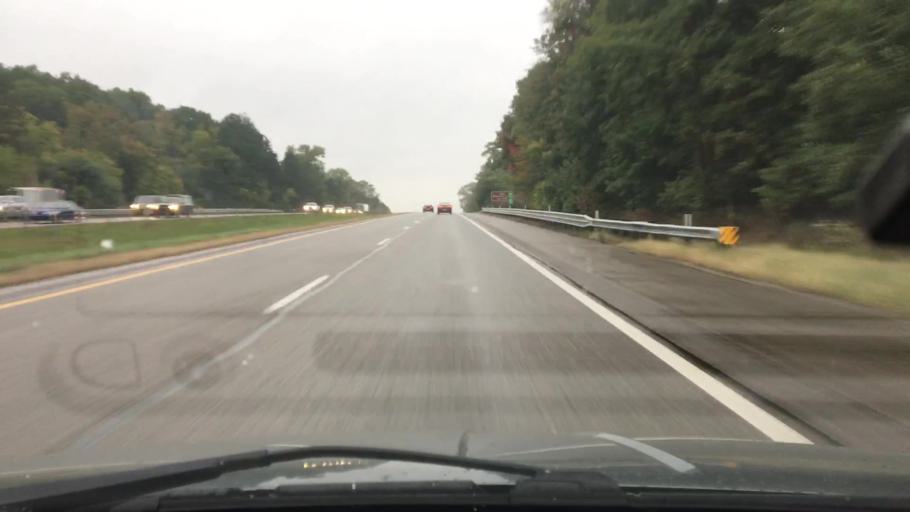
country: US
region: Michigan
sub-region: Washtenaw County
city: Chelsea
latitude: 42.2937
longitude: -84.0537
